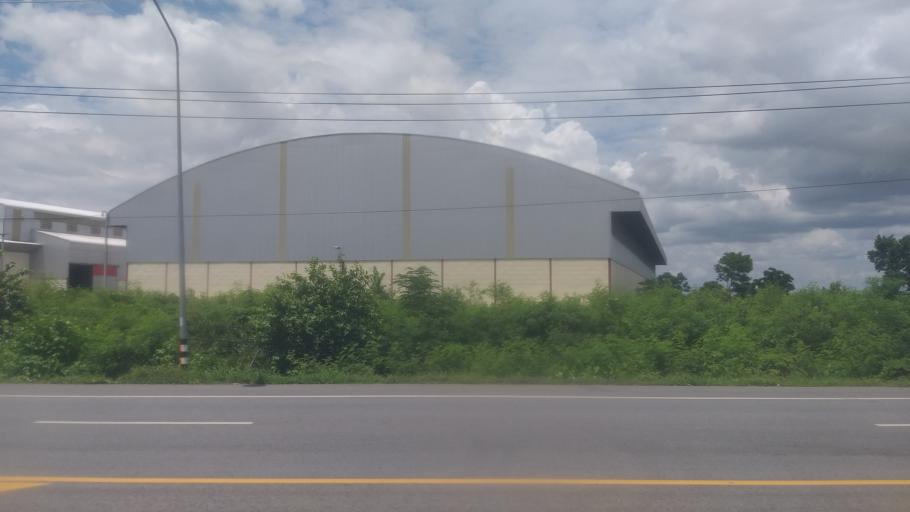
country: TH
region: Nakhon Ratchasima
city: Non Thai
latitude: 15.1052
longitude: 102.1028
